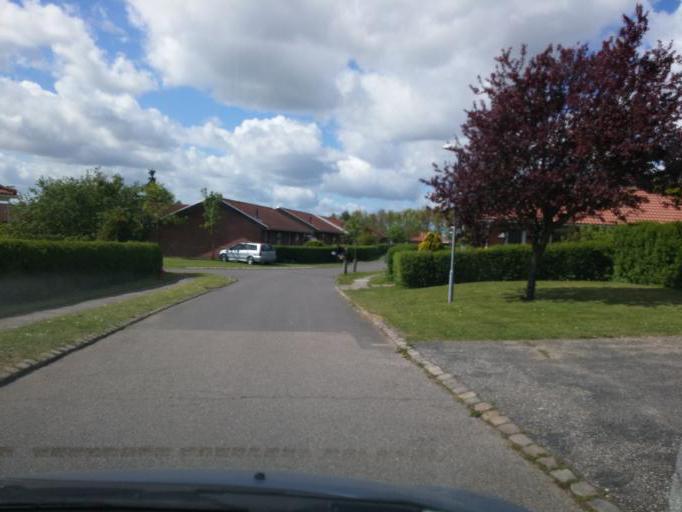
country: DK
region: South Denmark
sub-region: Kerteminde Kommune
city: Munkebo
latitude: 55.4464
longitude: 10.5376
